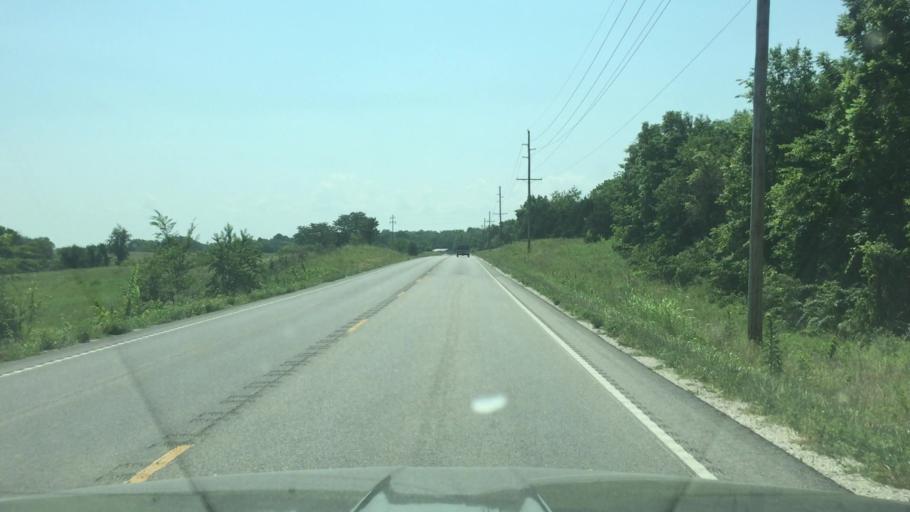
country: US
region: Missouri
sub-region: Miller County
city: Eldon
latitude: 38.3841
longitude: -92.6865
